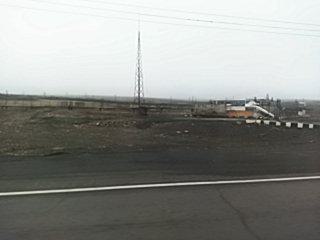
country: RU
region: Krasnoyarskiy
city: Kayyerkan
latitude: 69.3164
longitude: 87.9656
